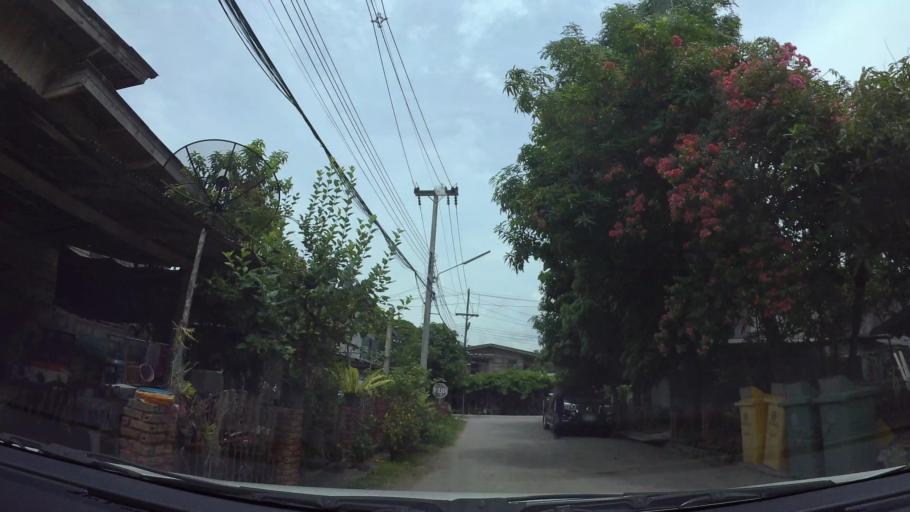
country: TH
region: Chiang Mai
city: Chiang Mai
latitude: 18.7866
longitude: 98.9757
